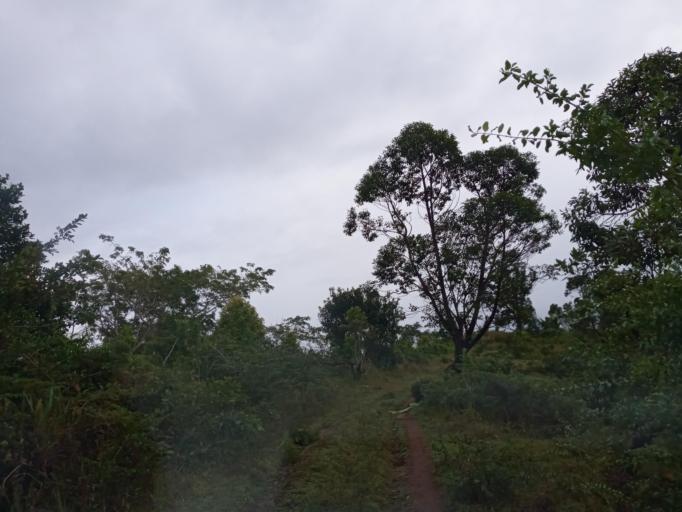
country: MG
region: Atsimo-Atsinanana
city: Vohipaho
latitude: -24.0125
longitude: 47.4155
